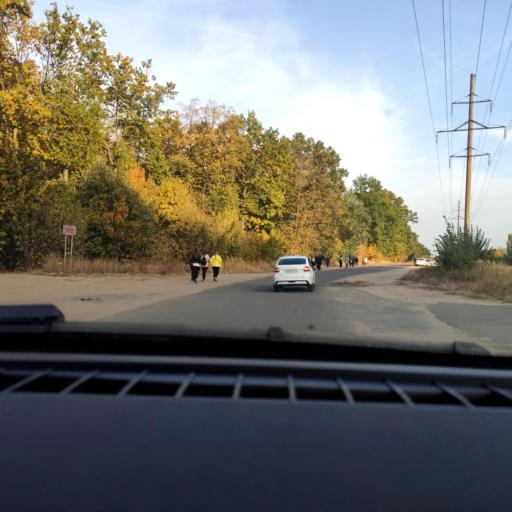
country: RU
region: Voronezj
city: Podgornoye
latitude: 51.7313
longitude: 39.2058
